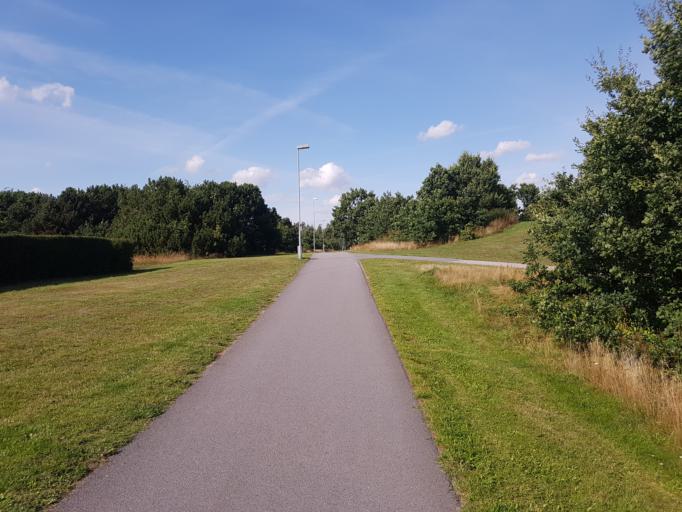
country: SE
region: Skane
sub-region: Sjobo Kommun
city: Sjoebo
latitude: 55.6402
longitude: 13.7000
